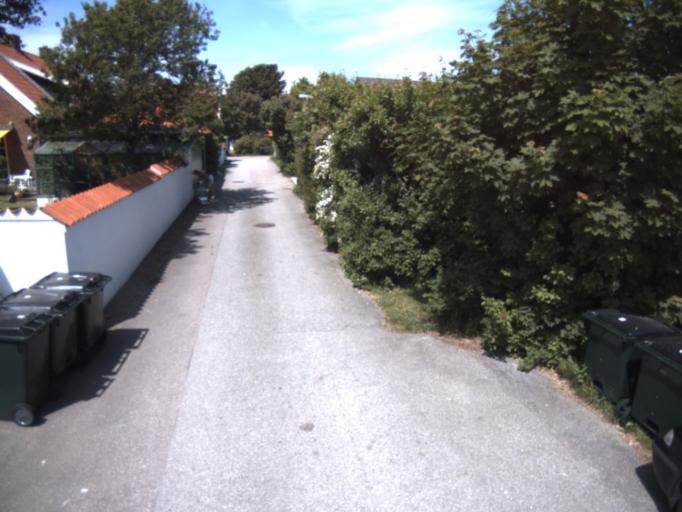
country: DK
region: Capital Region
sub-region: Helsingor Kommune
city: Hellebaek
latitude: 56.1174
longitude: 12.6066
